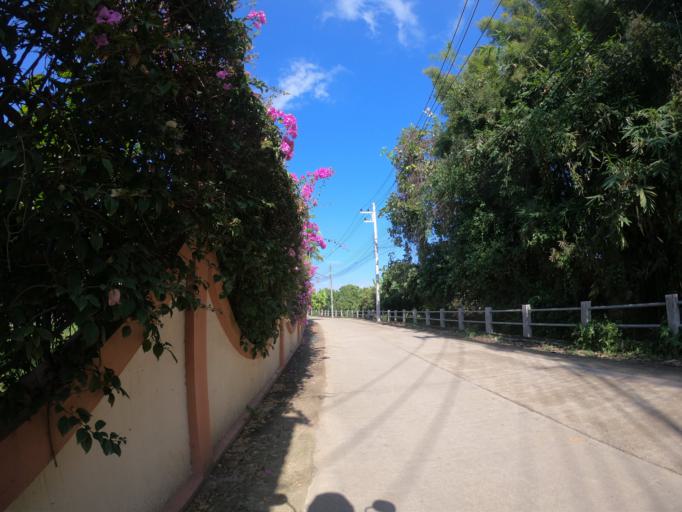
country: TH
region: Chiang Mai
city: Saraphi
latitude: 18.7122
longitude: 99.0207
